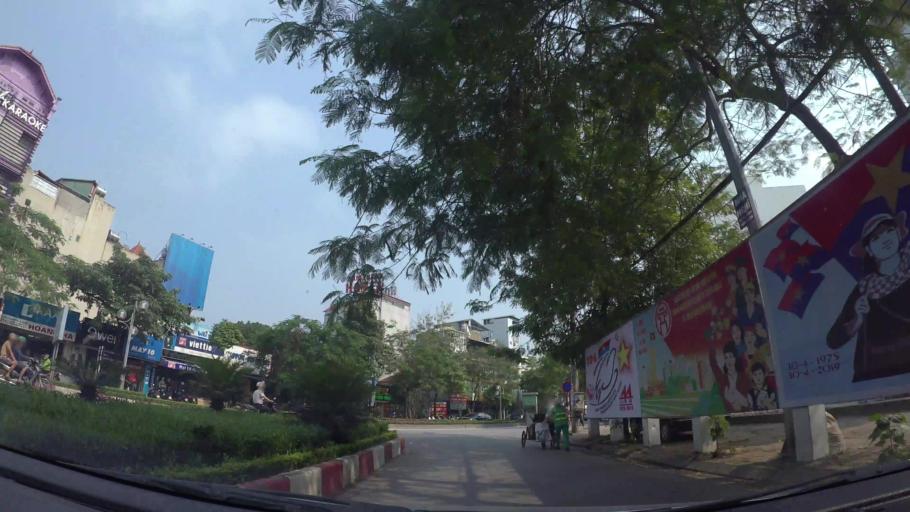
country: VN
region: Ha Noi
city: Tay Ho
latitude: 21.0609
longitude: 105.8089
